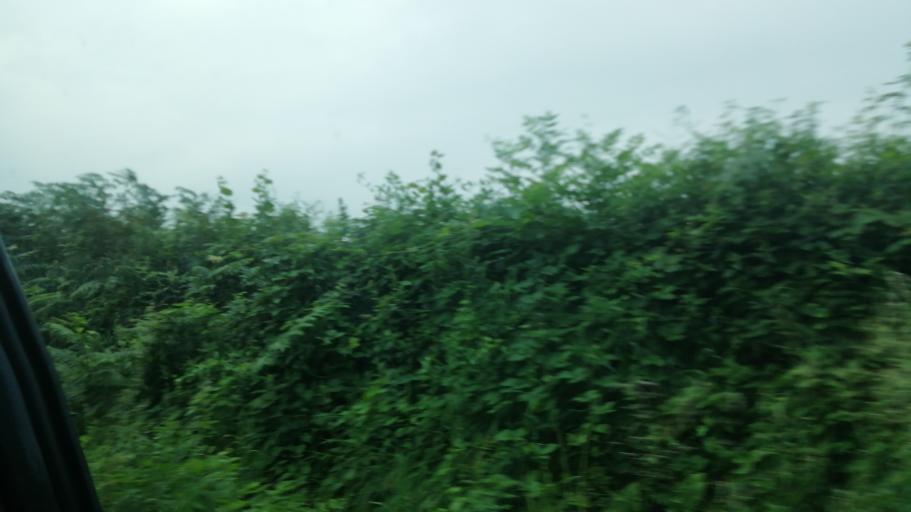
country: IE
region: Leinster
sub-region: Kilkenny
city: Callan
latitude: 52.5327
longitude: -7.5183
